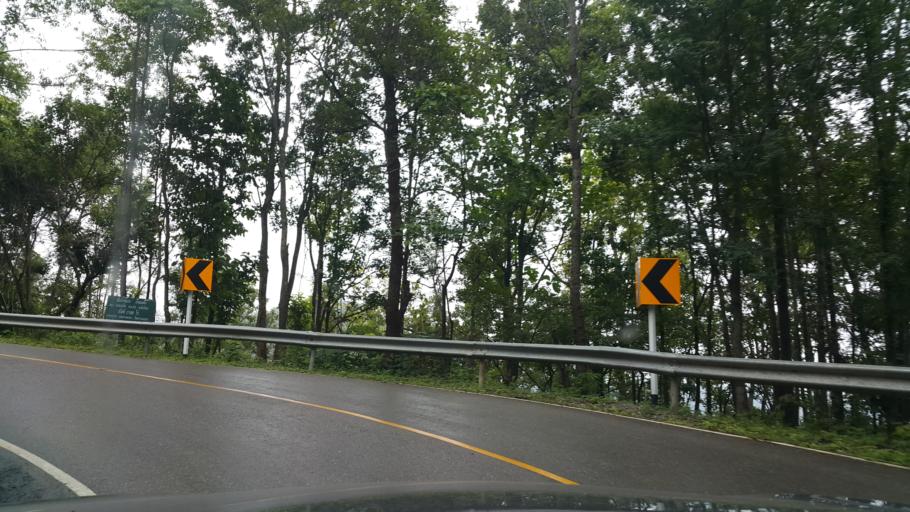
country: TH
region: Chiang Mai
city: Samoeng
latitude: 18.8585
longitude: 98.6730
